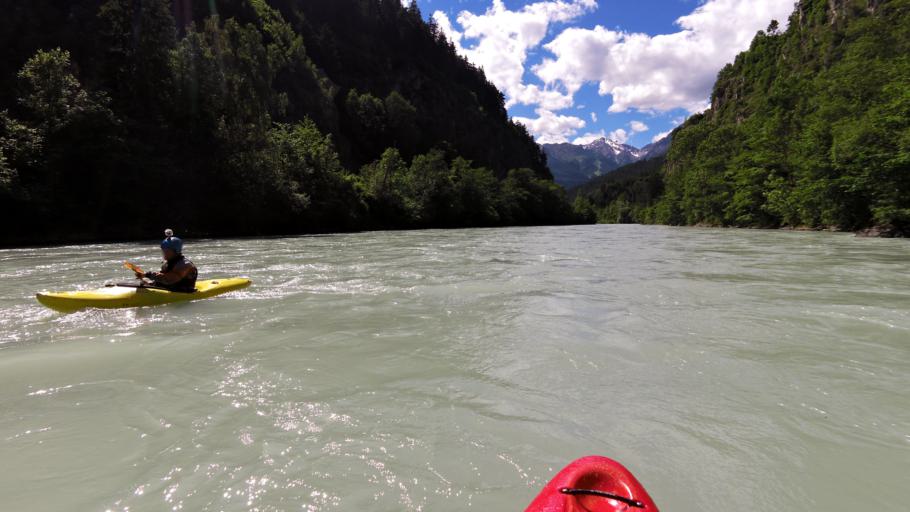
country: AT
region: Tyrol
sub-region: Politischer Bezirk Imst
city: Karres
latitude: 47.2142
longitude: 10.7786
